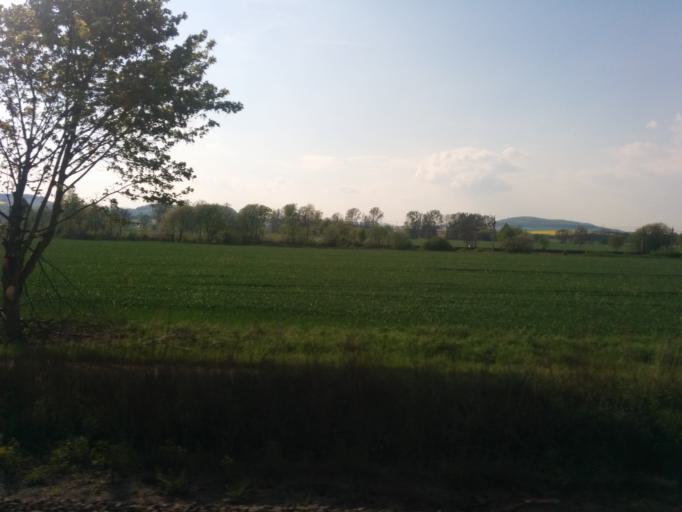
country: DE
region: Lower Saxony
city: Hillerse
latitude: 51.6830
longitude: 9.9736
